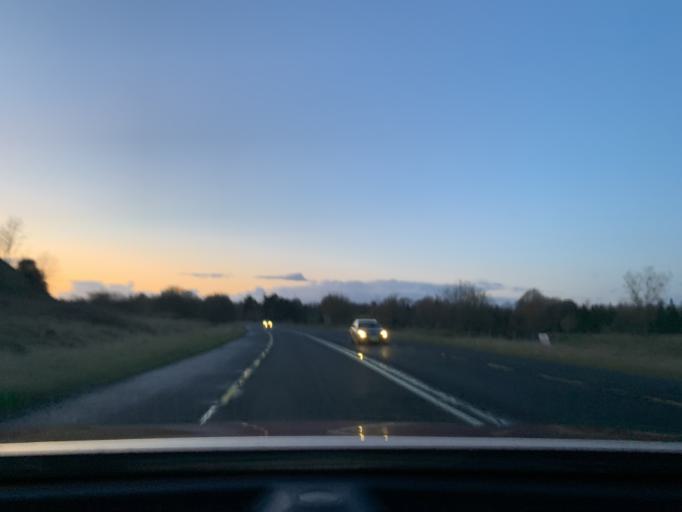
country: IE
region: Connaught
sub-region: County Leitrim
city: Carrick-on-Shannon
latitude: 53.9570
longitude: -8.1624
